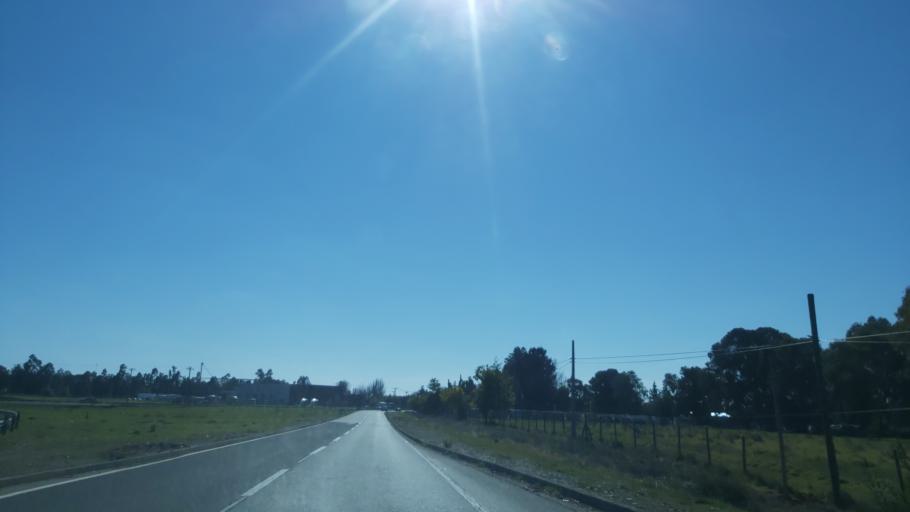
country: CL
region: Biobio
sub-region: Provincia de Nuble
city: Bulnes
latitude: -36.6553
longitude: -72.2274
